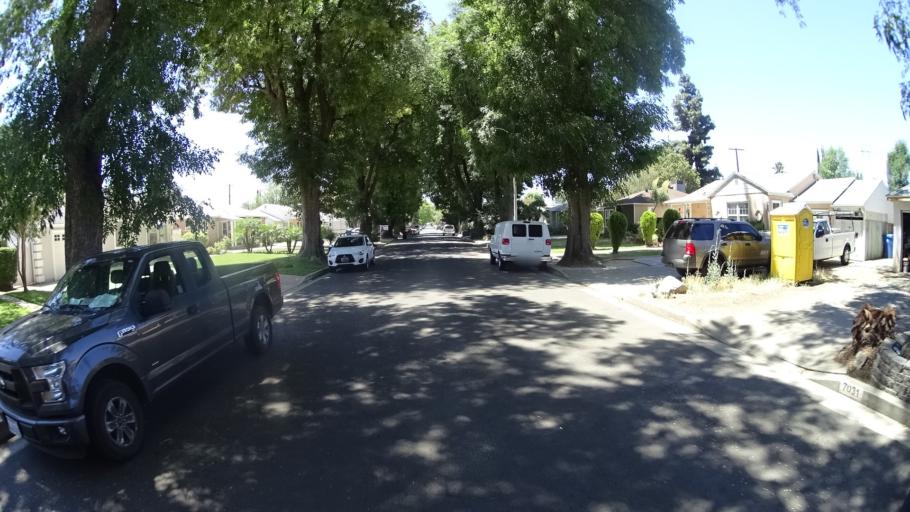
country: US
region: California
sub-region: Los Angeles County
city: Northridge
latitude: 34.1984
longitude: -118.5216
